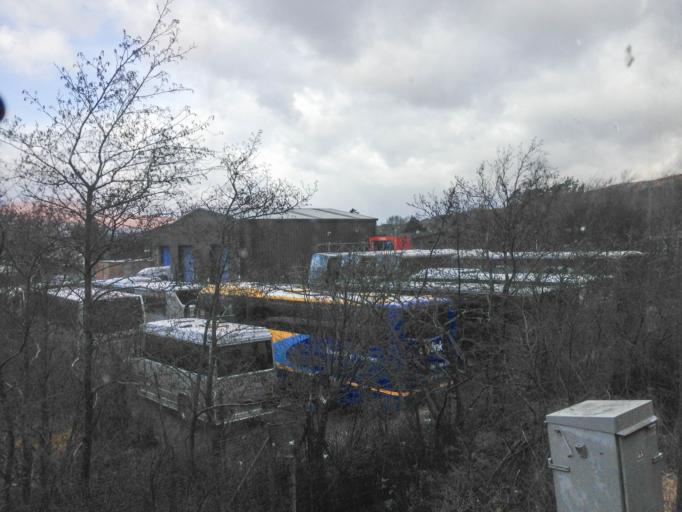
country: GB
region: Scotland
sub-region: Highland
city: Fort William
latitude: 56.8428
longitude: -5.0942
